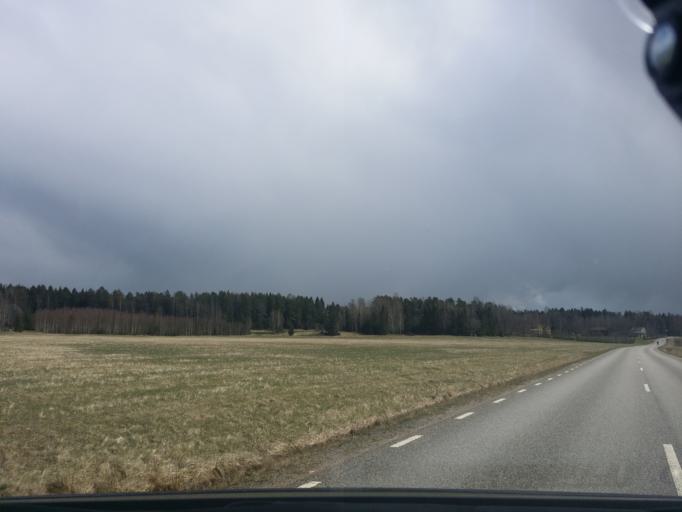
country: SE
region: Vaestmanland
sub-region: Sala Kommun
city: Sala
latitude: 59.9086
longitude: 16.6486
